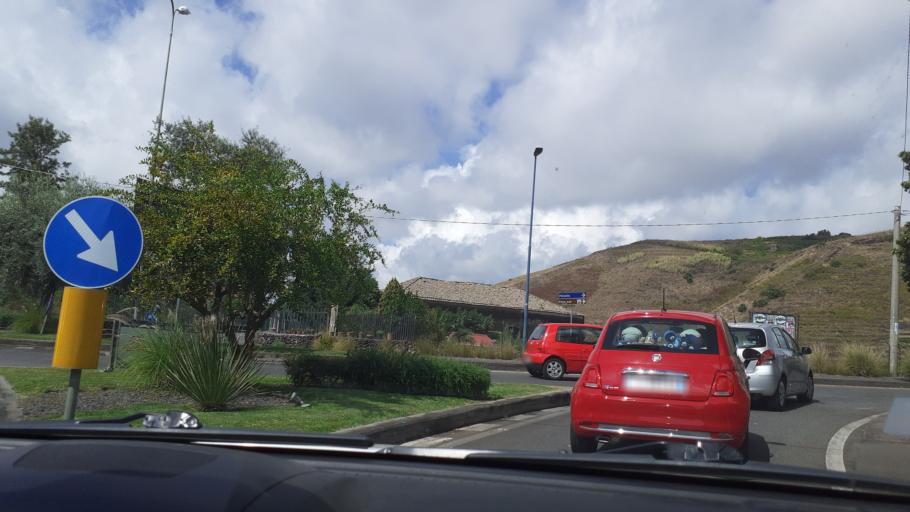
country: IT
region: Sicily
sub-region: Catania
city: Trecastagni
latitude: 37.6085
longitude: 15.0654
